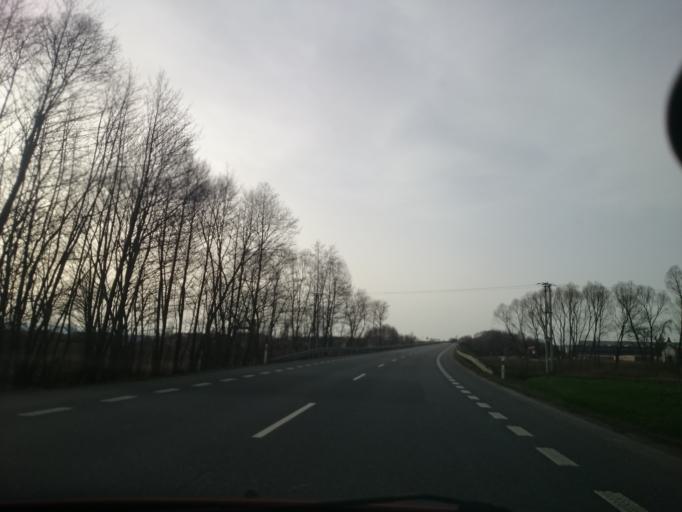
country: PL
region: Opole Voivodeship
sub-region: Powiat nyski
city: Paczkow
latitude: 50.4549
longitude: 16.9876
